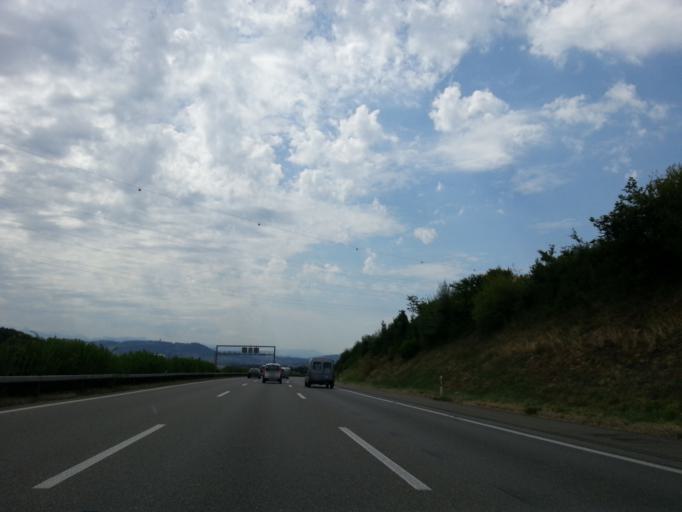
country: CH
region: Bern
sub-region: Bern-Mittelland District
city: Bolligen
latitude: 46.9939
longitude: 7.4833
